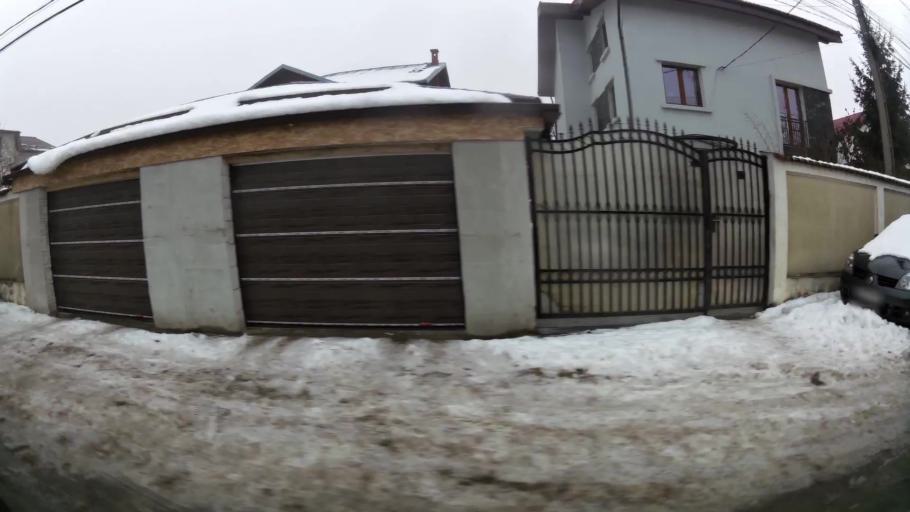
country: RO
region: Ilfov
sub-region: Comuna Chiajna
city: Chiajna
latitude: 44.4559
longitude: 25.9797
